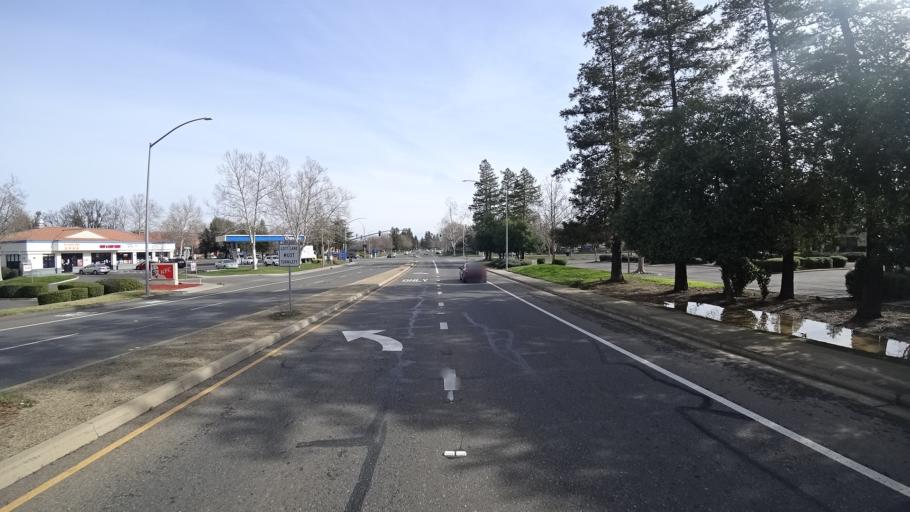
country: US
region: California
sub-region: Yolo County
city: Davis
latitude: 38.5398
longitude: -121.7326
